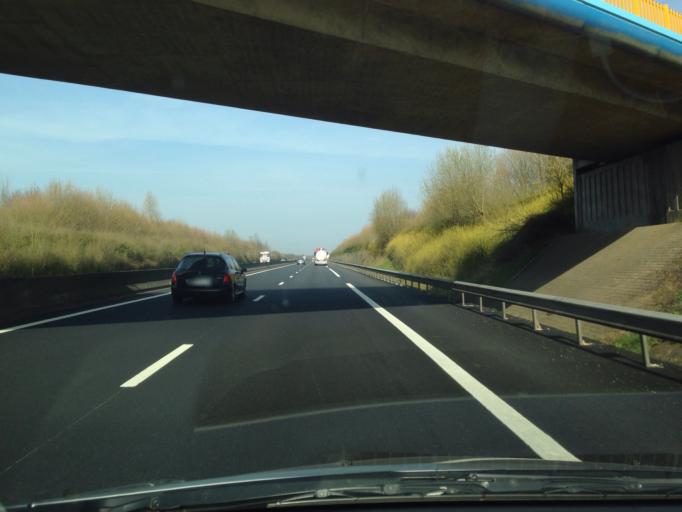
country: FR
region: Picardie
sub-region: Departement de la Somme
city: Oisemont
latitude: 50.0220
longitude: 1.7262
